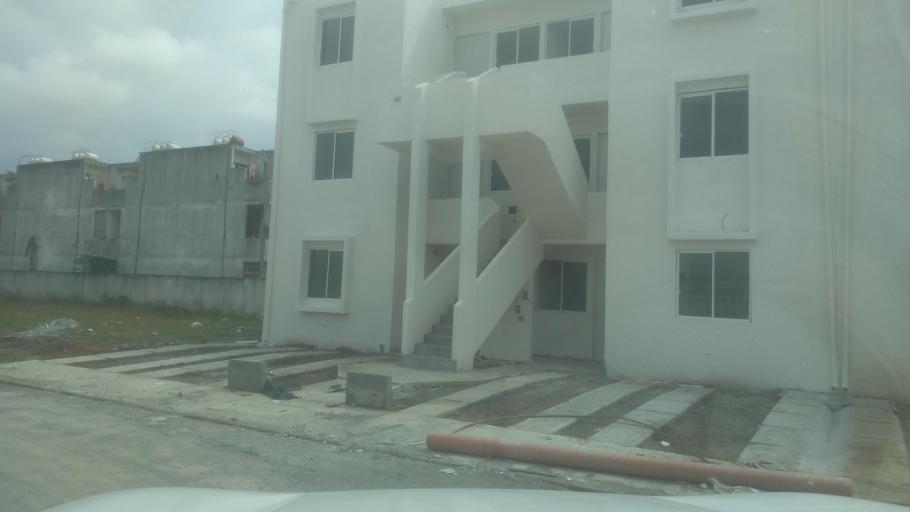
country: MX
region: Veracruz
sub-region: Medellin
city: Fraccionamiento Arboledas San Ramon
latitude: 19.0930
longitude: -96.1666
